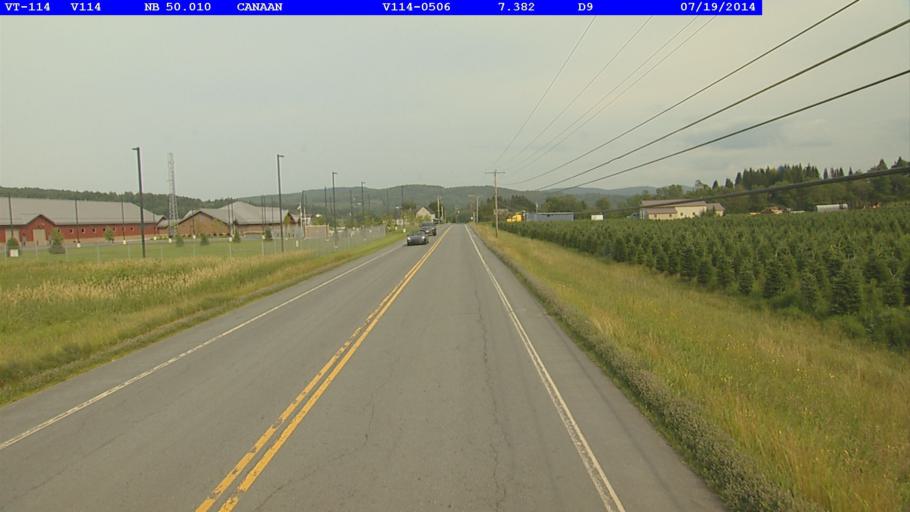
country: US
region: New Hampshire
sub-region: Coos County
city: Colebrook
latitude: 45.0030
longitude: -71.5515
